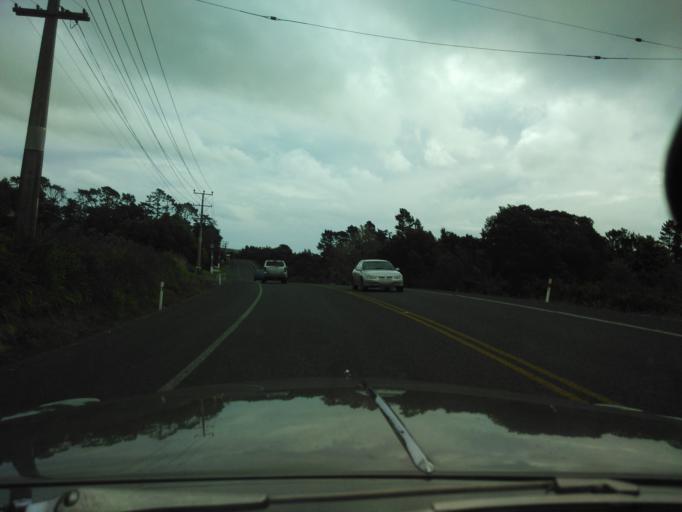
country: NZ
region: Auckland
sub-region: Auckland
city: Muriwai Beach
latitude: -36.7671
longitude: 174.5221
